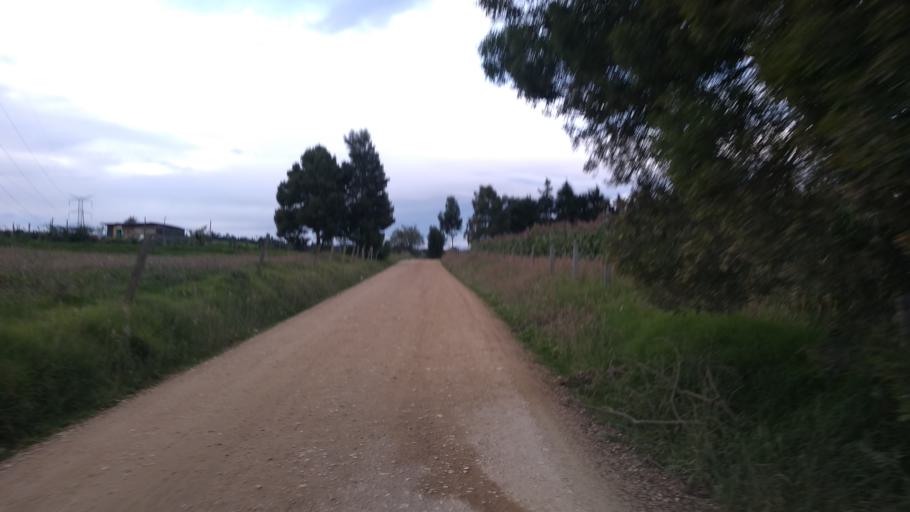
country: CO
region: Boyaca
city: Toca
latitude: 5.6165
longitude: -73.1712
